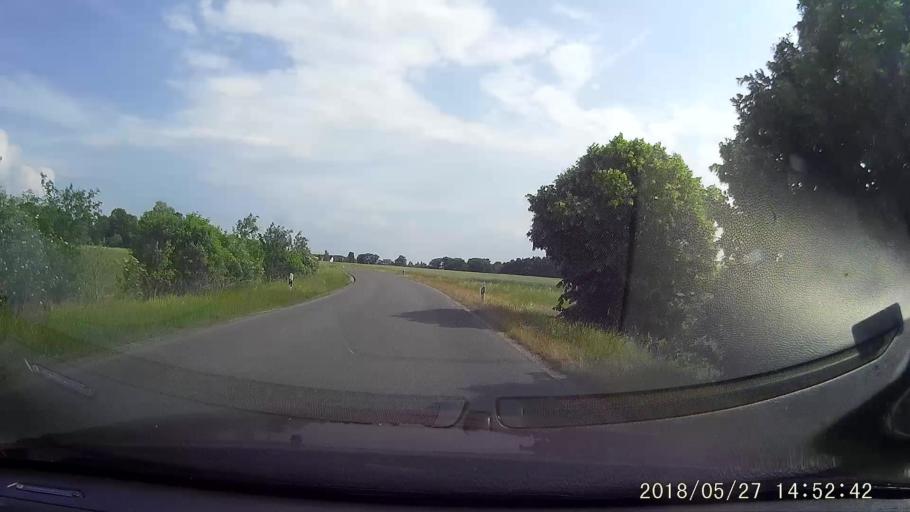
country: DE
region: Saxony
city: Klitten
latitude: 51.3551
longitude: 14.5835
